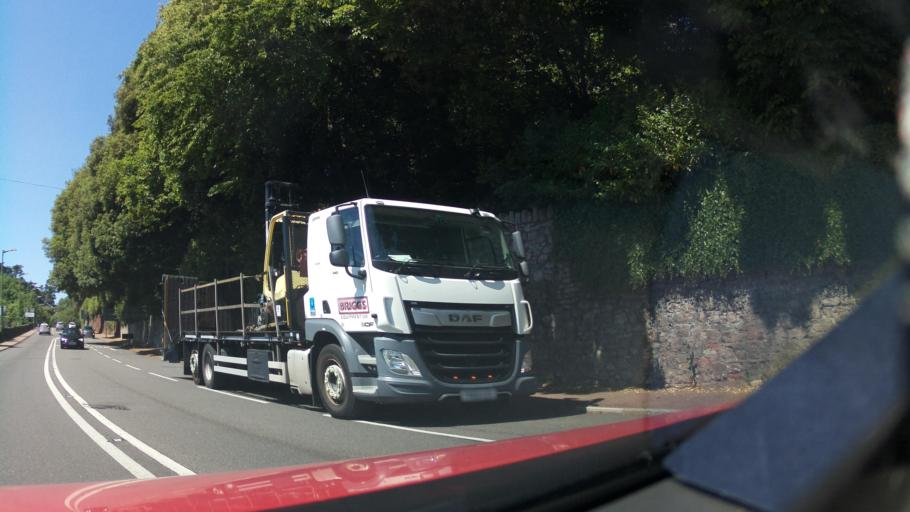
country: GB
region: England
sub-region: Borough of Torbay
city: Torquay
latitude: 50.4734
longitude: -3.5464
